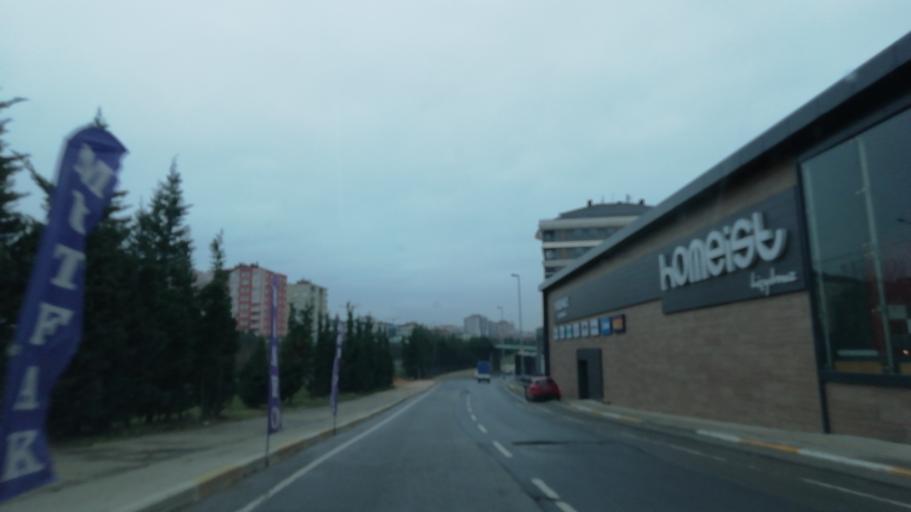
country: TR
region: Istanbul
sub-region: Atasehir
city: Atasehir
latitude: 41.0081
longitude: 29.0822
